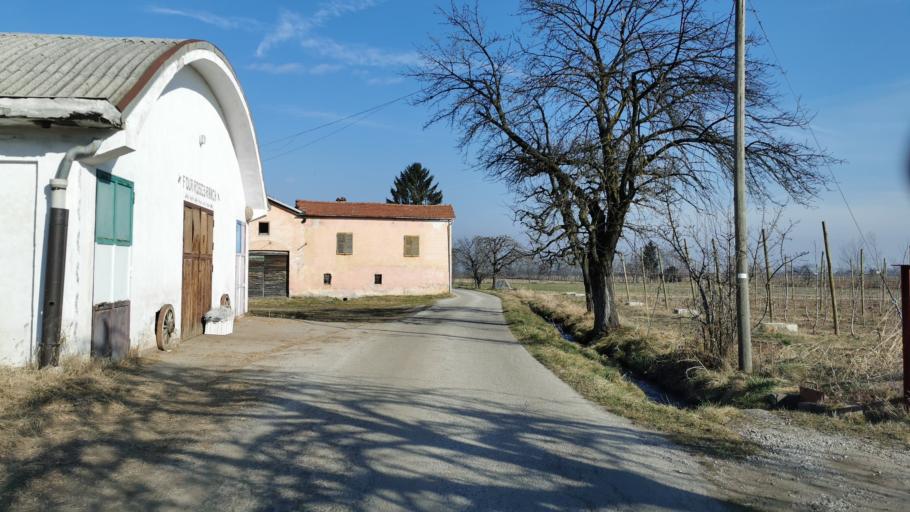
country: IT
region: Piedmont
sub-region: Provincia di Cuneo
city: Caraglio
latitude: 44.4419
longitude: 7.4436
